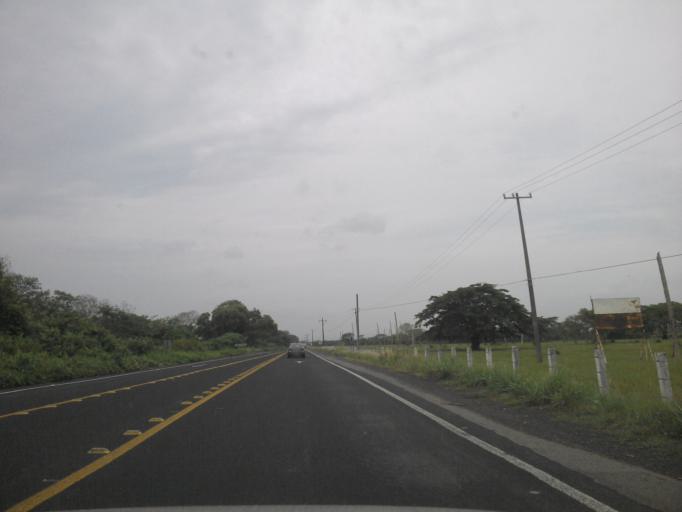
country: MX
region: Veracruz
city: Nautla
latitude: 20.2309
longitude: -96.7897
